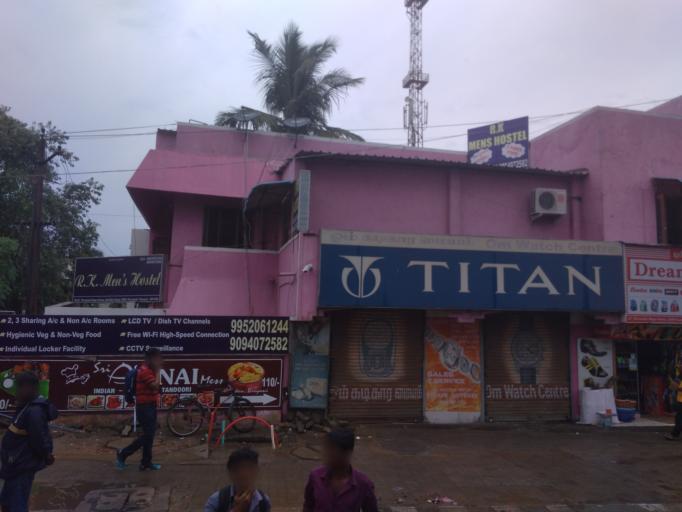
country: IN
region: Tamil Nadu
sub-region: Kancheepuram
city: Perungudi
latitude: 12.9591
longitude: 80.2443
